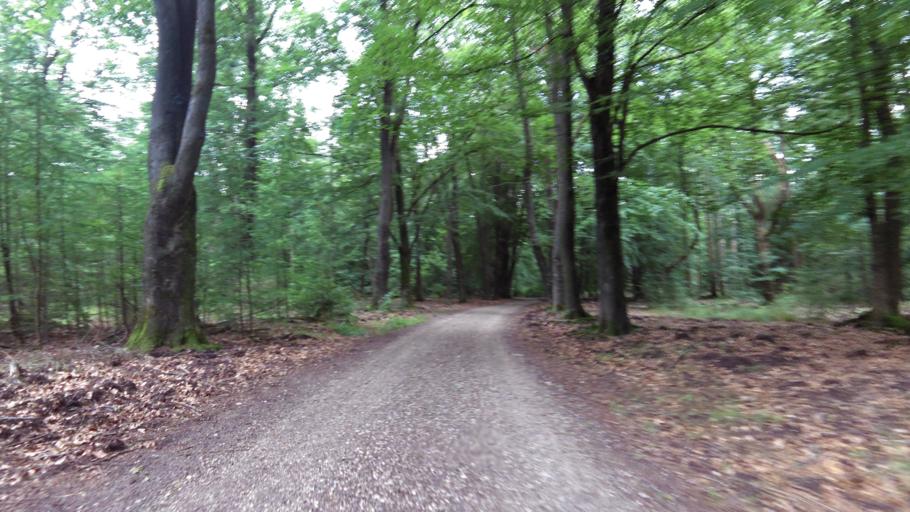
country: NL
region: Gelderland
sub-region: Gemeente Apeldoorn
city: Apeldoorn
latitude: 52.2223
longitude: 5.9037
